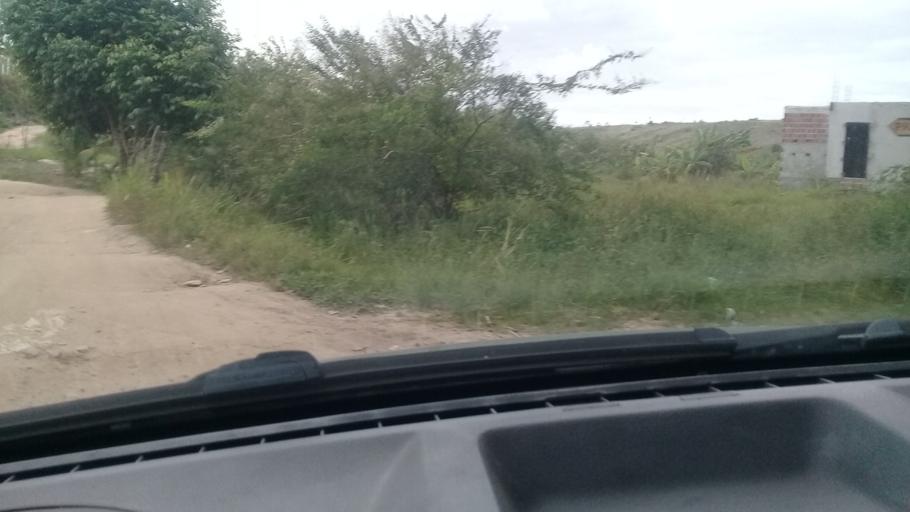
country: BR
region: Pernambuco
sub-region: Jaboatao Dos Guararapes
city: Jaboatao dos Guararapes
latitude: -8.0820
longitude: -35.0346
